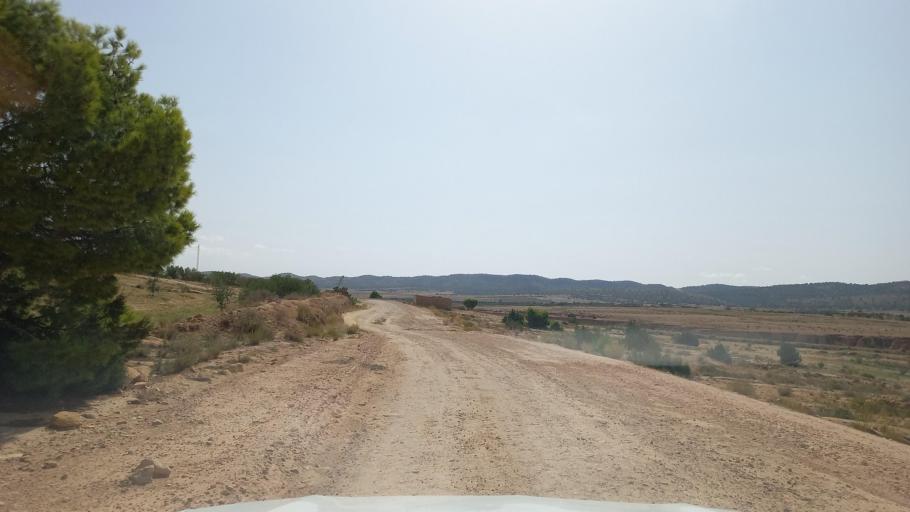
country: TN
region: Al Qasrayn
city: Sbiba
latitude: 35.3946
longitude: 8.9517
